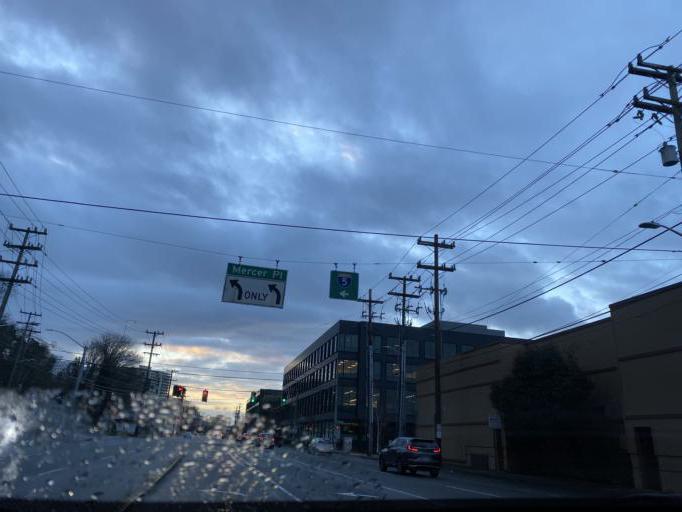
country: US
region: Washington
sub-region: King County
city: Seattle
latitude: 47.6280
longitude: -122.3670
